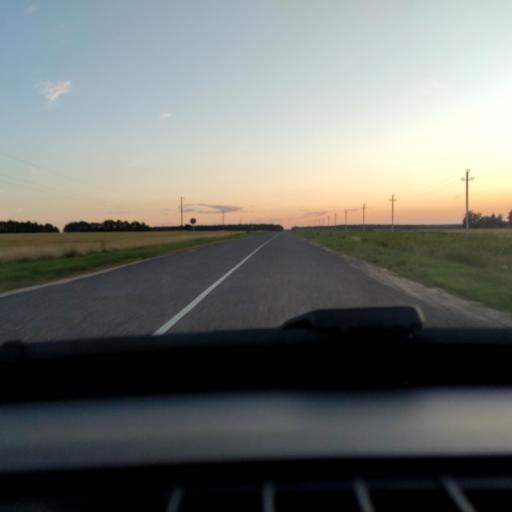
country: RU
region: Lipetsk
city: Zadonsk
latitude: 52.3114
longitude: 38.9094
